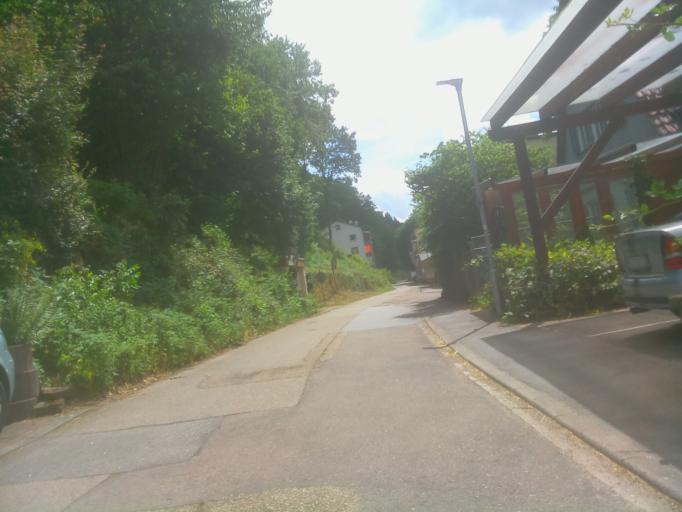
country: DE
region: Hesse
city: Hirschhorn
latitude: 49.4453
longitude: 8.9012
